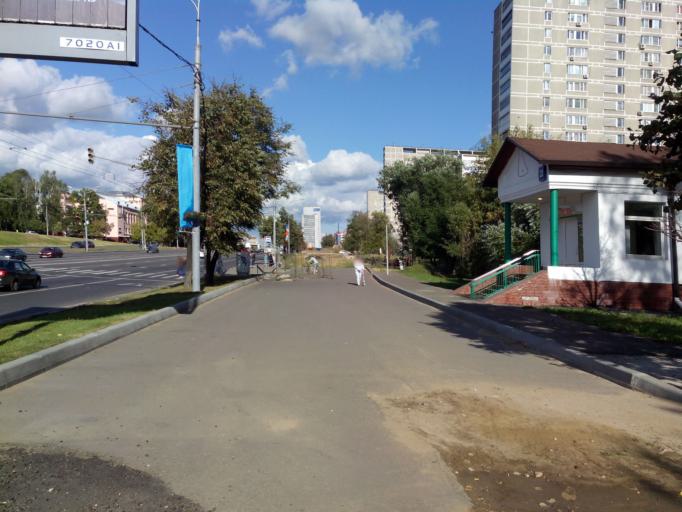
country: RU
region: Moskovskaya
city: Bogorodskoye
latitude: 55.7990
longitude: 37.7332
